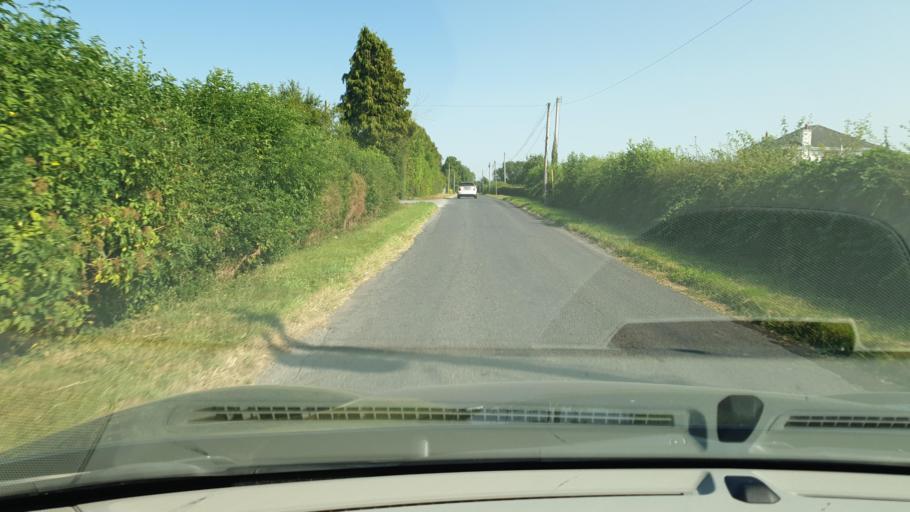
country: IE
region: Leinster
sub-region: An Mhi
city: Athboy
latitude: 53.6325
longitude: -6.9689
